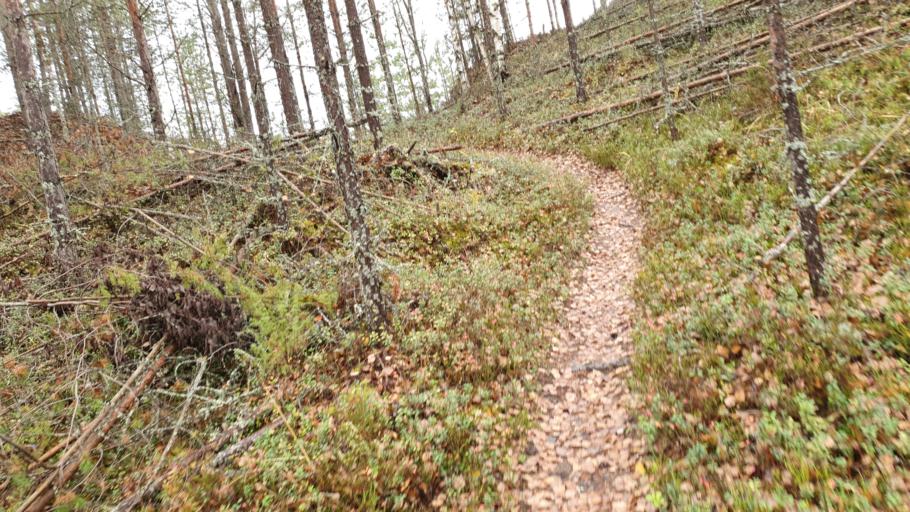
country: FI
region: Kainuu
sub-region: Kehys-Kainuu
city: Kuhmo
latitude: 64.1512
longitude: 29.3964
